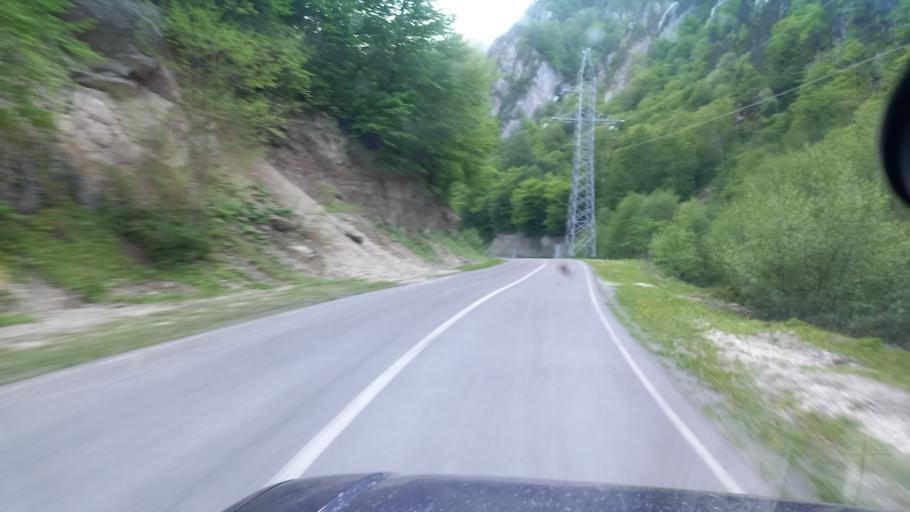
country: RU
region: North Ossetia
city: Tarskoye
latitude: 42.8901
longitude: 44.9395
